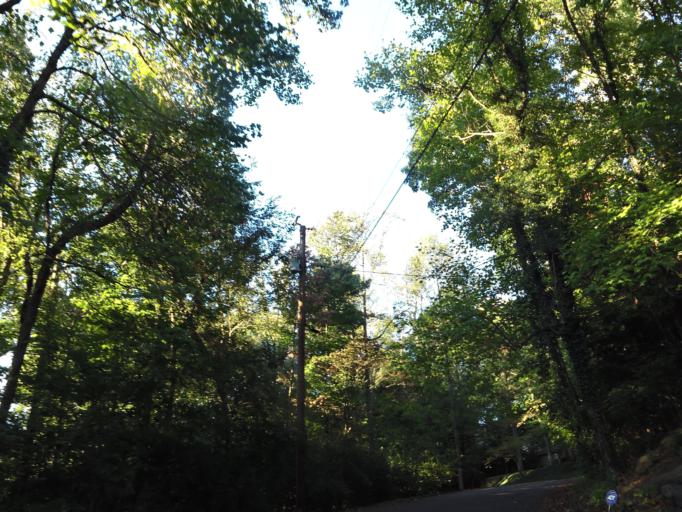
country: US
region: Tennessee
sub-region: Knox County
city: Knoxville
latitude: 35.9257
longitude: -83.9490
